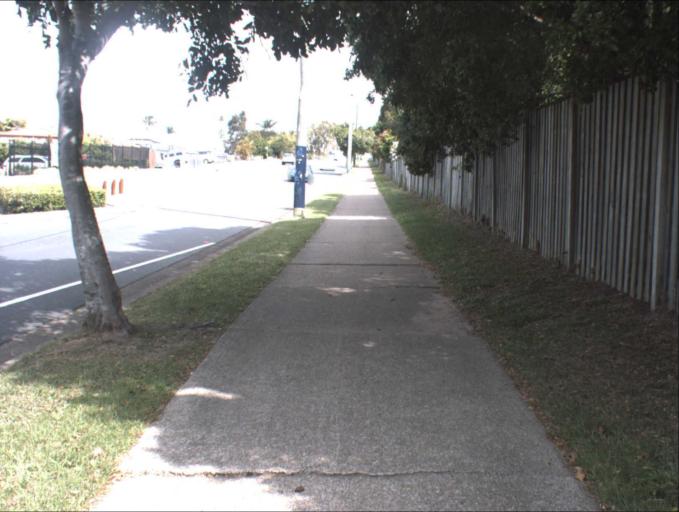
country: AU
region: Queensland
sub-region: Logan
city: Park Ridge South
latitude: -27.6739
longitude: 153.0524
